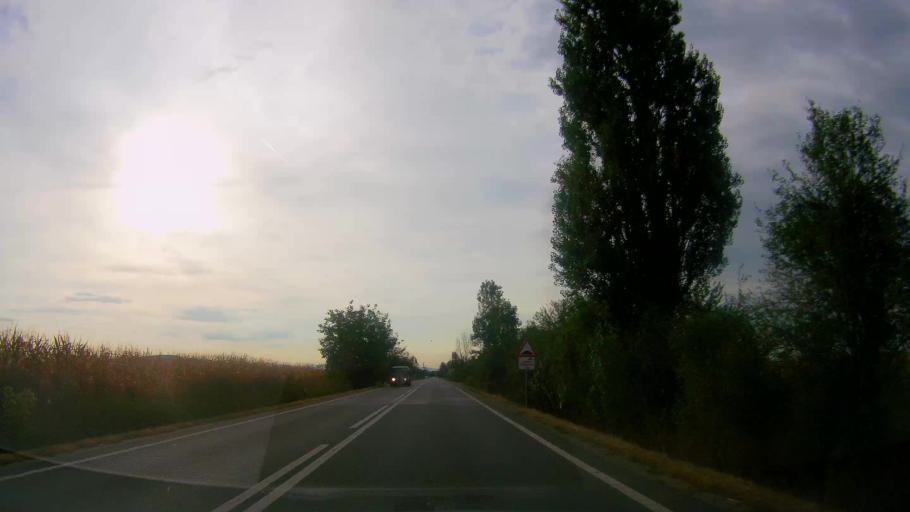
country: RO
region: Satu Mare
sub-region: Comuna Turulung
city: Turulung
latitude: 47.9495
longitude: 23.0681
